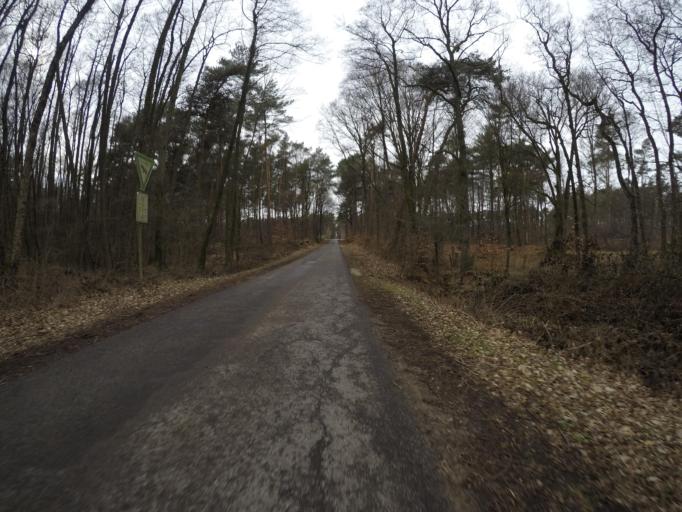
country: DE
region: North Rhine-Westphalia
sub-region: Regierungsbezirk Dusseldorf
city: Bocholt
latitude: 51.7824
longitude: 6.6471
